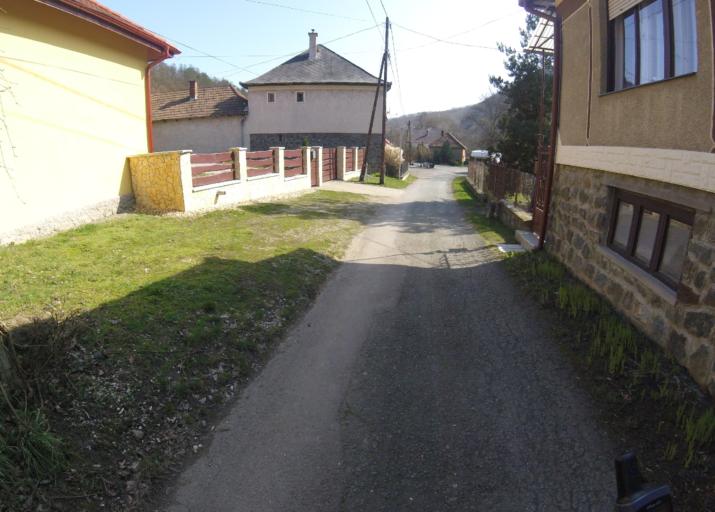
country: HU
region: Heves
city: Belapatfalva
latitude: 47.9893
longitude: 20.3302
